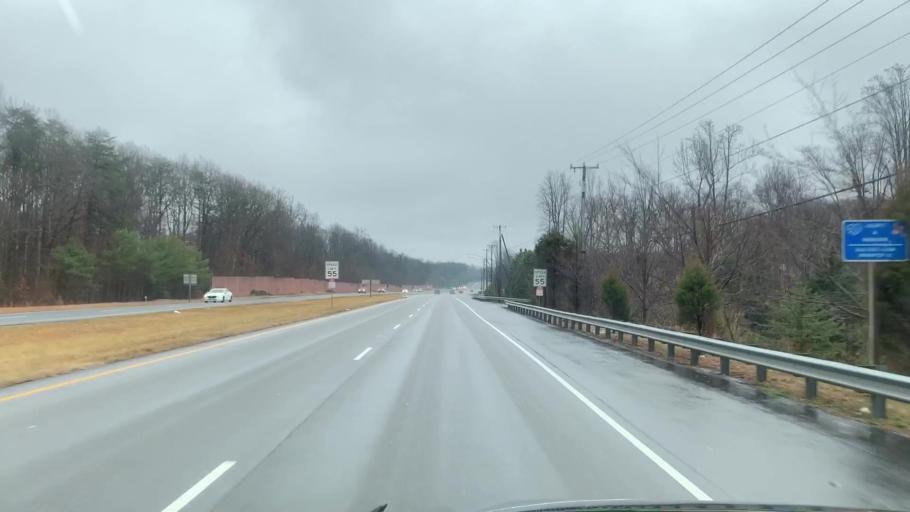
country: US
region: Virginia
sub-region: Fairfax County
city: Burke
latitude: 38.7519
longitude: -77.2998
